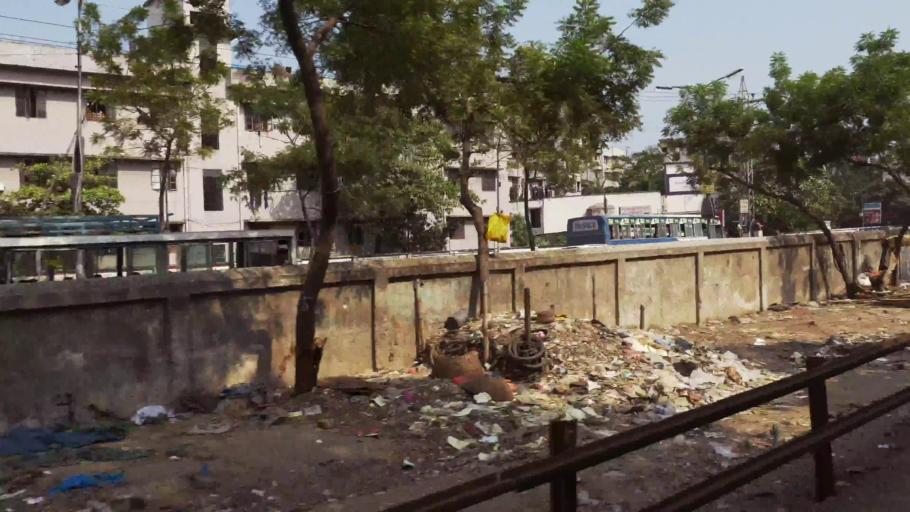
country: BD
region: Dhaka
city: Paltan
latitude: 23.7494
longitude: 90.4142
